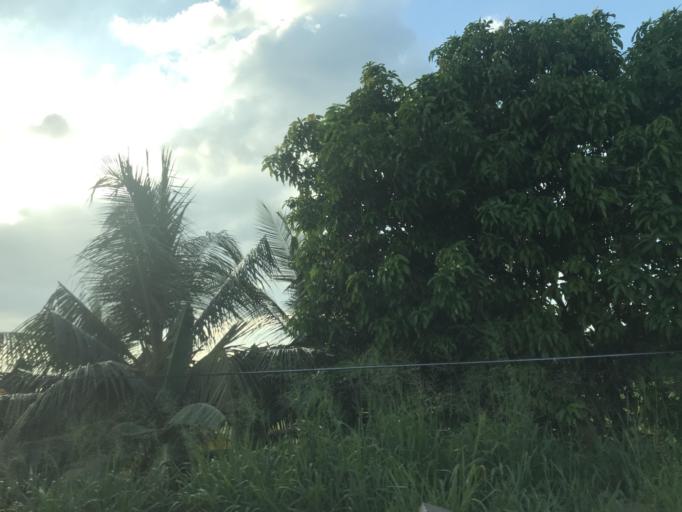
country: LK
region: Western
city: Gampaha
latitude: 7.0982
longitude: 79.9913
